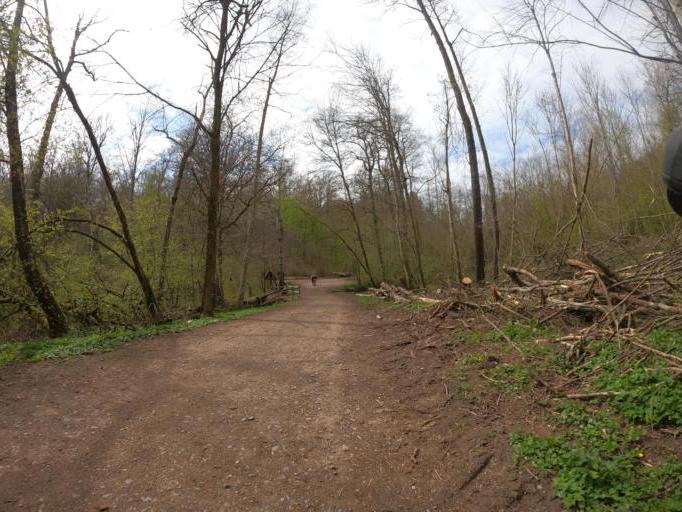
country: DE
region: Baden-Wuerttemberg
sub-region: Tuebingen Region
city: Wannweil
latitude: 48.5079
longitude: 9.1403
